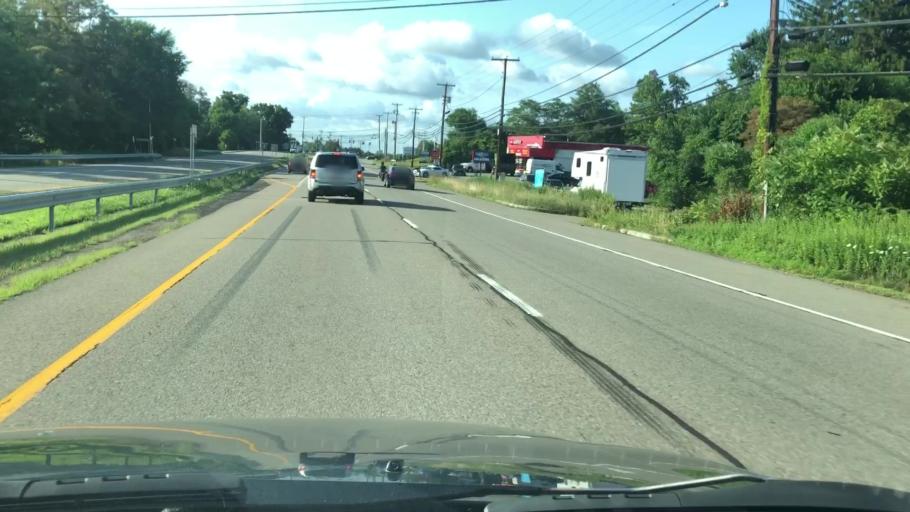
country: US
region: New York
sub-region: Dutchess County
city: Wappingers Falls
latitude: 41.5708
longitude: -73.9087
